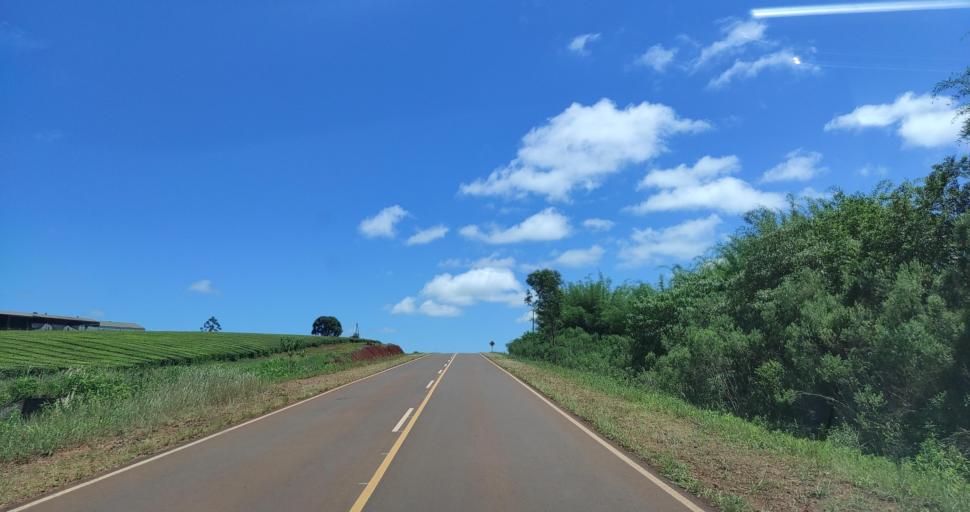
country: AR
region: Misiones
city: Campo Grande
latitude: -27.3134
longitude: -54.8993
